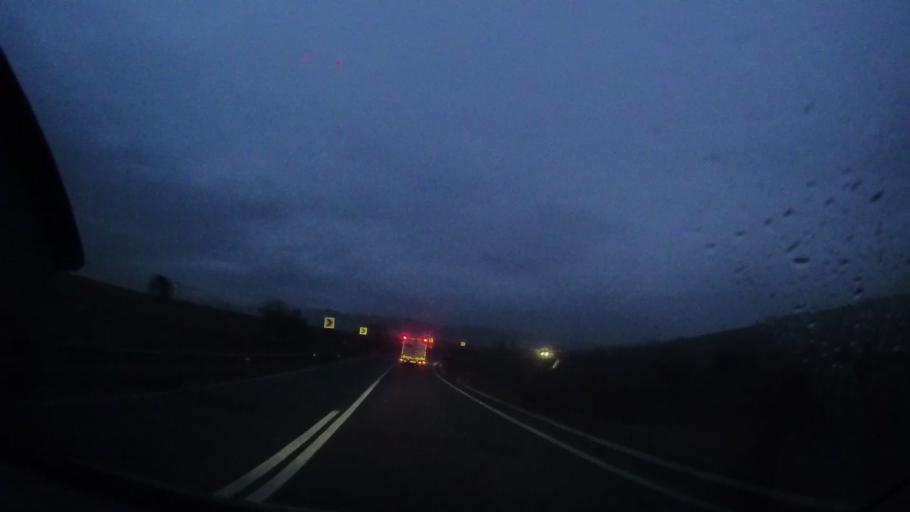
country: RO
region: Harghita
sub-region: Comuna Subcetate
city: Subcetate
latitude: 46.8548
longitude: 25.4706
